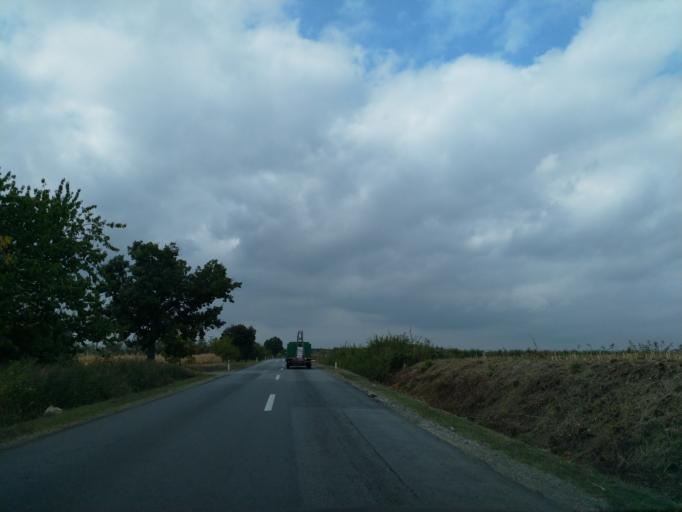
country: RS
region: Central Serbia
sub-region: Sumadijski Okrug
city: Kragujevac
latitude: 44.1198
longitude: 20.8323
